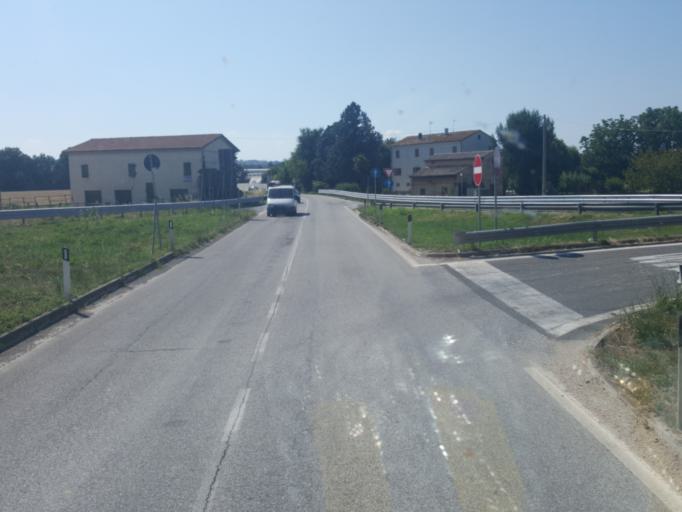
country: IT
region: The Marches
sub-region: Provincia di Ancona
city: Borghetto
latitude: 43.5540
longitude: 13.2994
